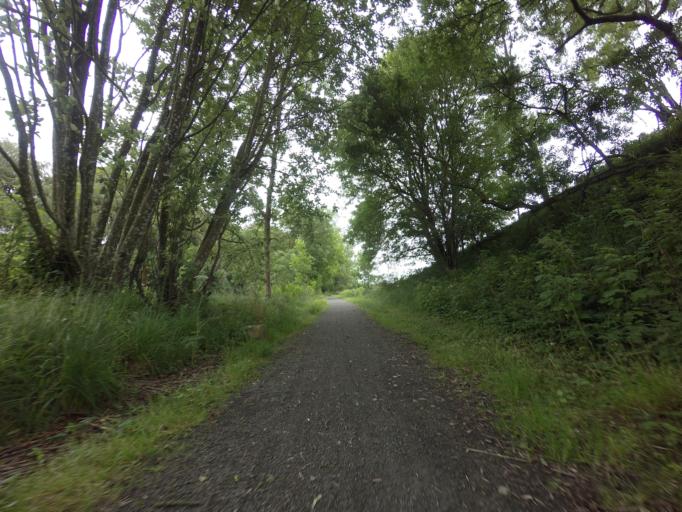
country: GB
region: Scotland
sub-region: Aberdeenshire
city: Mintlaw
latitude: 57.5120
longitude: -2.1405
